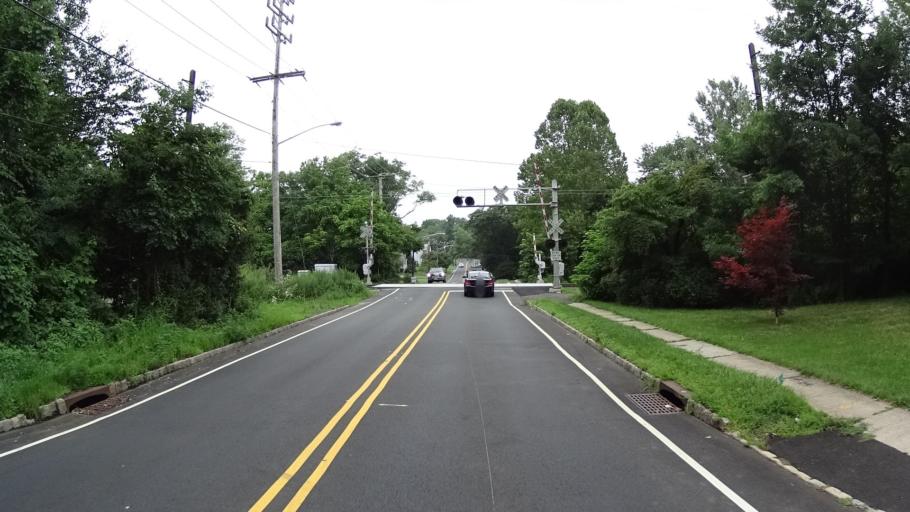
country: US
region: New Jersey
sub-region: Union County
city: New Providence
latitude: 40.6875
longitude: -74.4164
